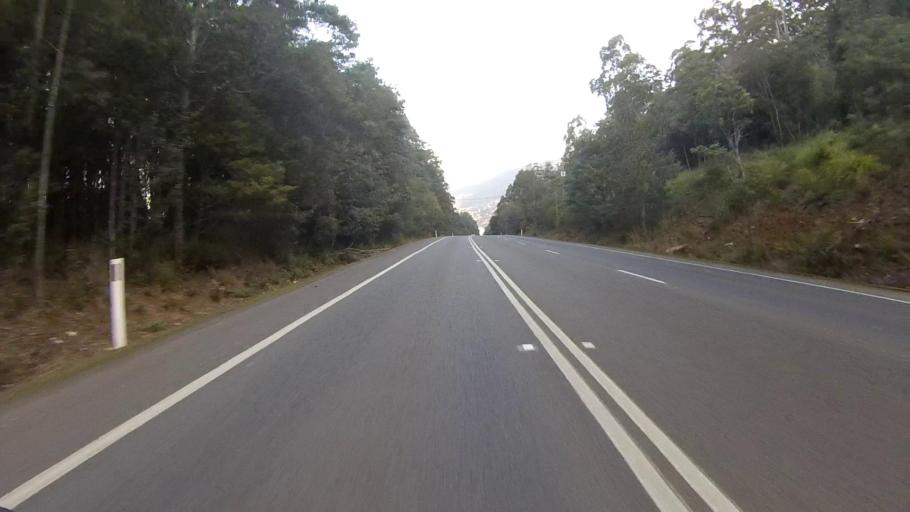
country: AU
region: Tasmania
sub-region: Sorell
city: Sorell
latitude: -43.0001
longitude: 147.9267
